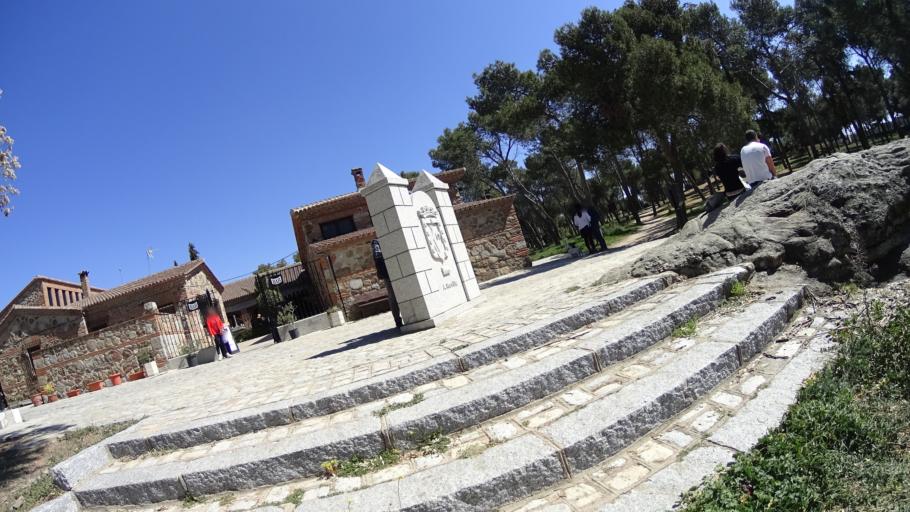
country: ES
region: Madrid
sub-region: Provincia de Madrid
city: Colmenar Viejo
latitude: 40.7026
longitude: -3.7699
